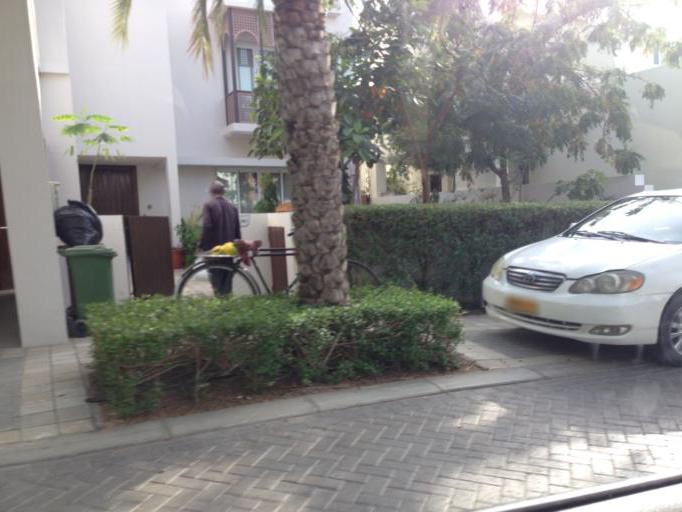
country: OM
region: Muhafazat Masqat
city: As Sib al Jadidah
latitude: 23.6238
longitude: 58.2710
